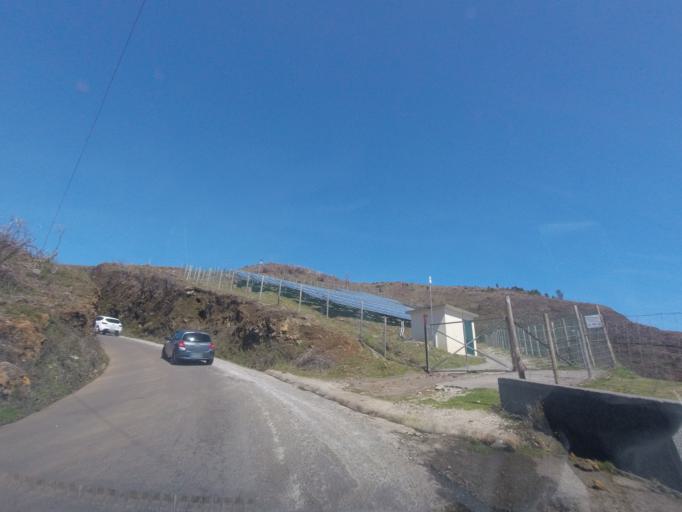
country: PT
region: Madeira
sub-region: Calheta
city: Arco da Calheta
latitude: 32.7324
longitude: -17.1034
